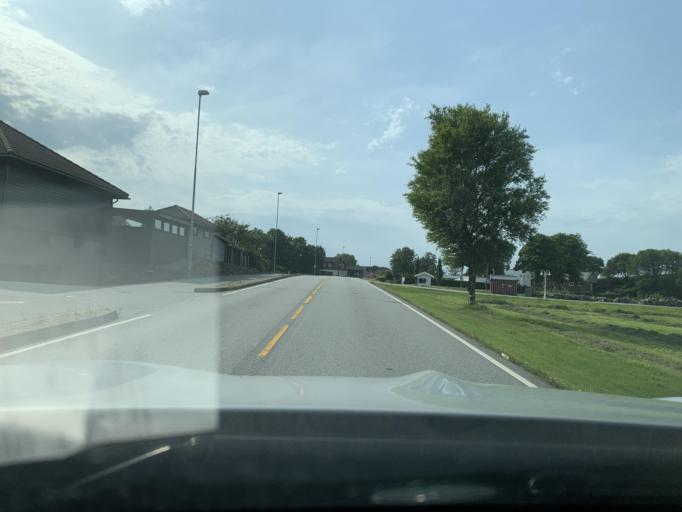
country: NO
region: Rogaland
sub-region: Time
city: Bryne
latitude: 58.7377
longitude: 5.6334
